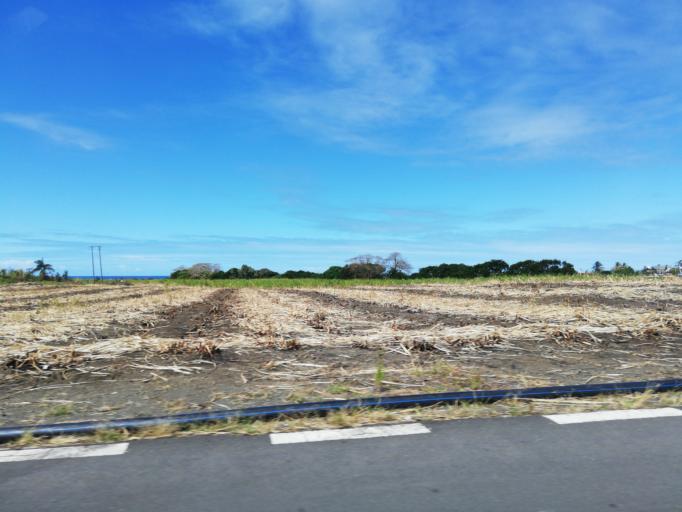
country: MU
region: Grand Port
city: Plaine Magnien
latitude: -20.4563
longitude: 57.6770
